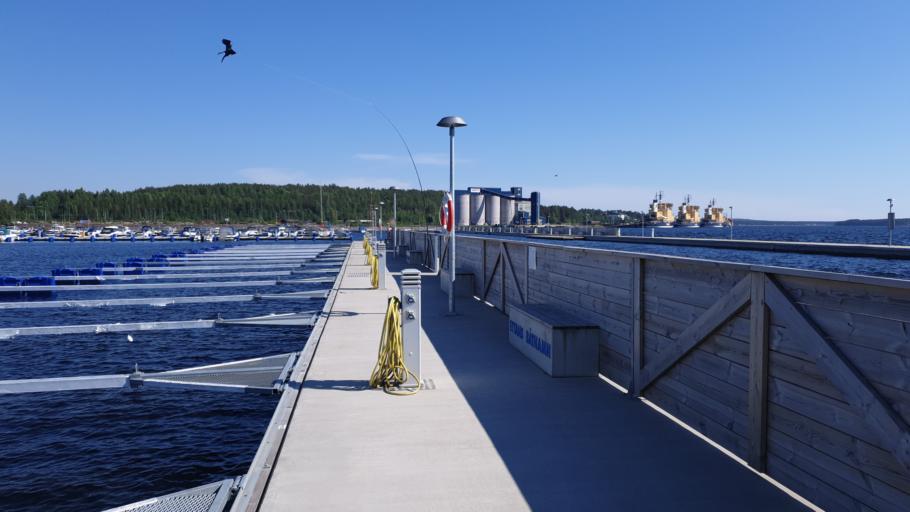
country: SE
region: Norrbotten
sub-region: Lulea Kommun
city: Lulea
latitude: 65.5785
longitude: 22.1616
